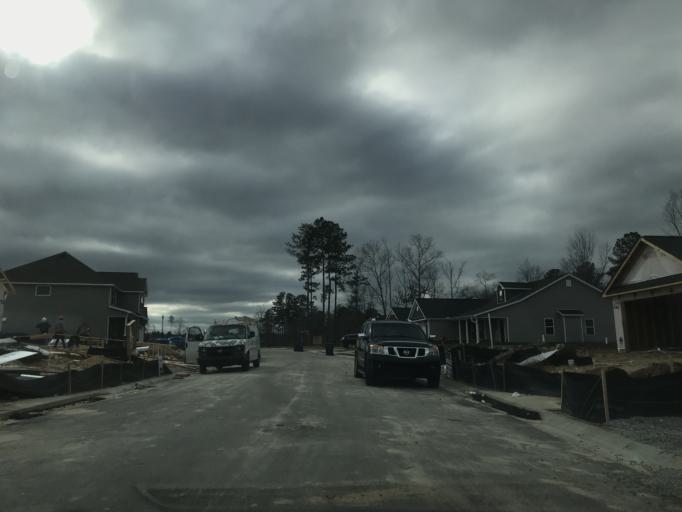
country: US
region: Georgia
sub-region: Columbia County
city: Grovetown
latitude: 33.4476
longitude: -82.1454
